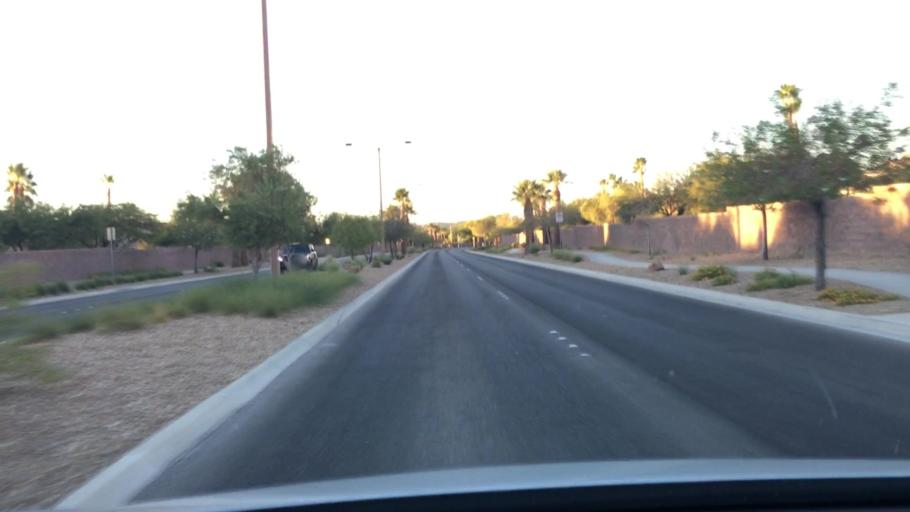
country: US
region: Nevada
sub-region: Clark County
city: Summerlin South
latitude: 36.1380
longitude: -115.3424
